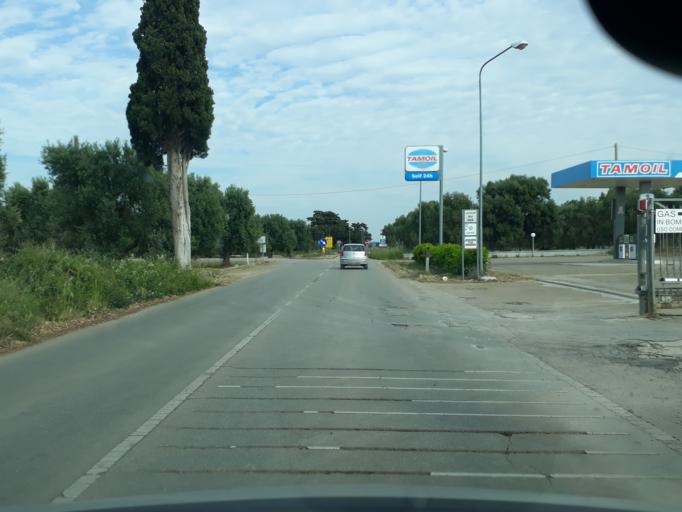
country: IT
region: Apulia
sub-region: Provincia di Brindisi
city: Pezze di Greco
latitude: 40.8064
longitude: 17.4269
